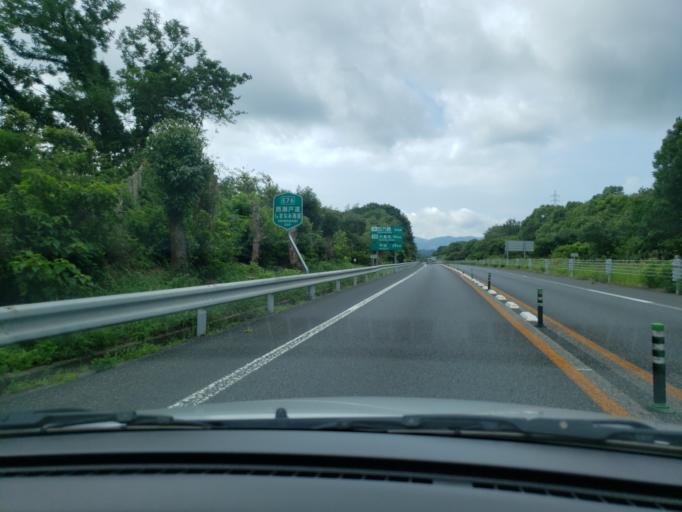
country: JP
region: Hiroshima
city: Innoshima
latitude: 34.2426
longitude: 133.0478
